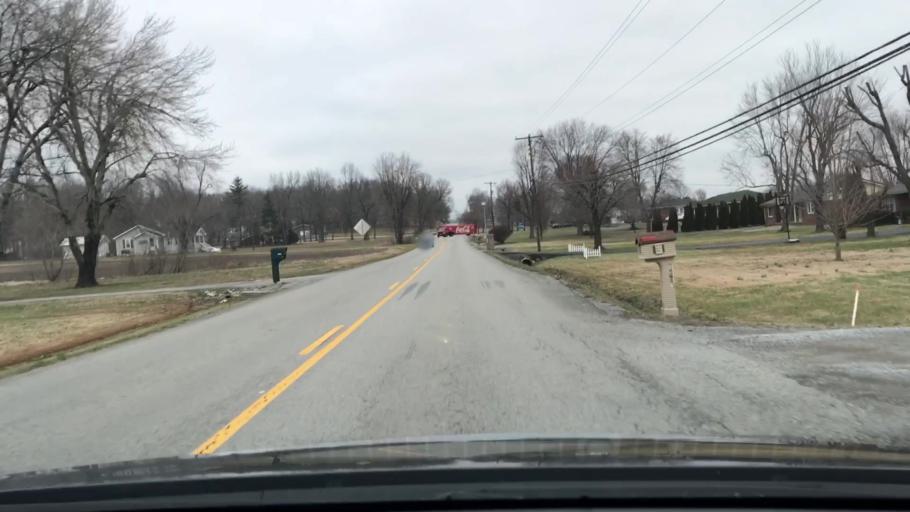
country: US
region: Kentucky
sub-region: Muhlenberg County
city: Greenville
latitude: 37.2218
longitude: -87.1938
